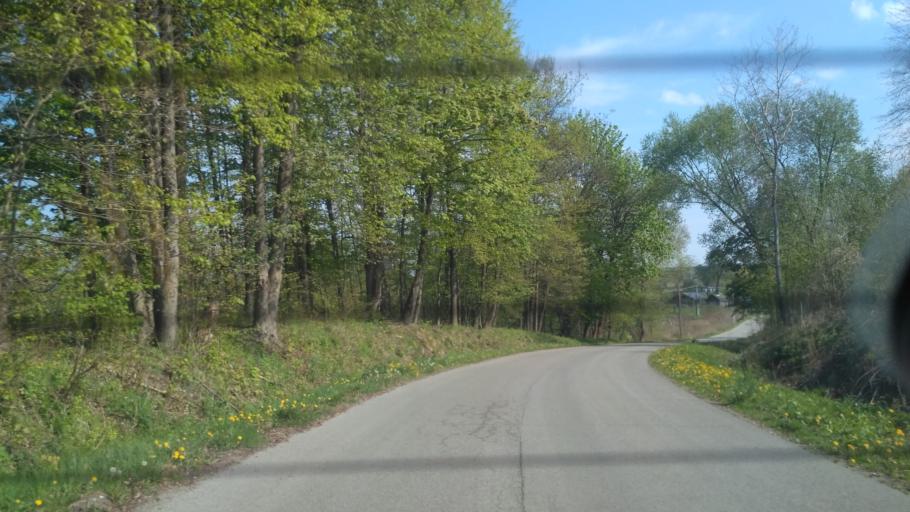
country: PL
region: Subcarpathian Voivodeship
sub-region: Powiat lubaczowski
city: Wielkie Oczy
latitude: 49.9733
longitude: 23.0602
